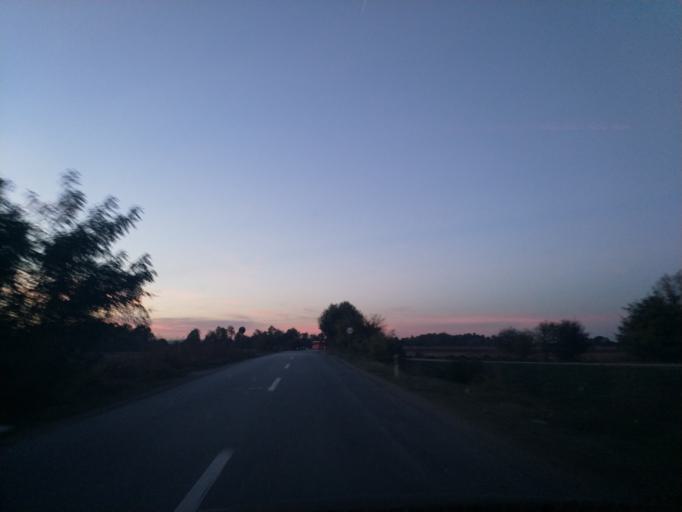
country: RS
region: Central Serbia
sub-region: Pomoravski Okrug
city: Svilajnac
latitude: 44.2351
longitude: 21.1379
